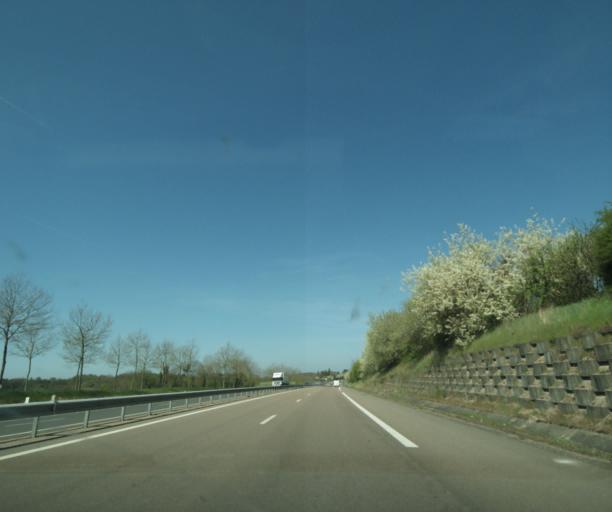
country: FR
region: Bourgogne
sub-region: Departement de la Nievre
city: Pougues-les-Eaux
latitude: 47.0992
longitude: 3.0773
